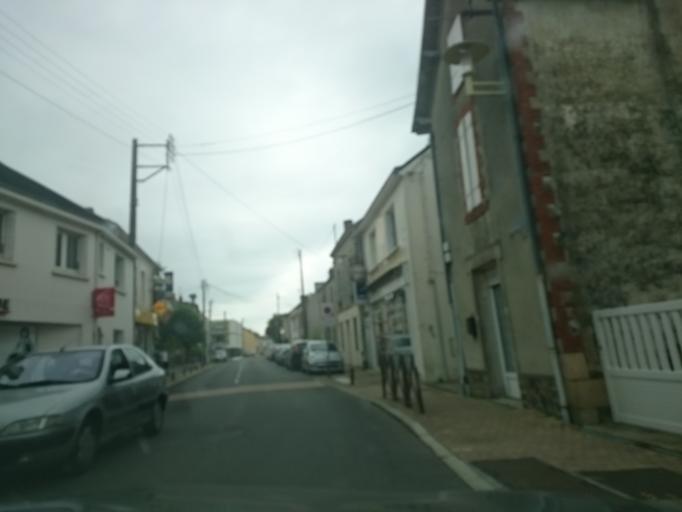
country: FR
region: Pays de la Loire
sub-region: Departement de la Loire-Atlantique
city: Le Pellerin
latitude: 47.1995
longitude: -1.7530
